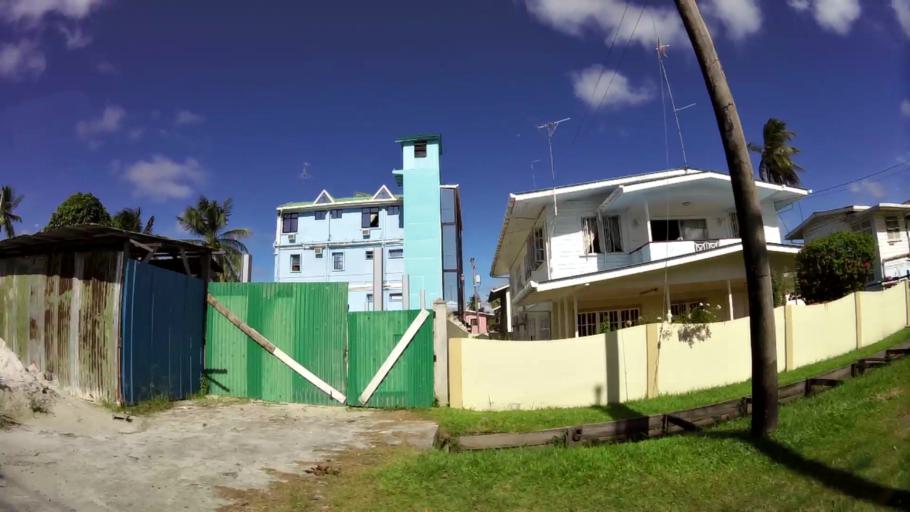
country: GY
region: Demerara-Mahaica
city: Georgetown
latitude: 6.8188
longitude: -58.1330
